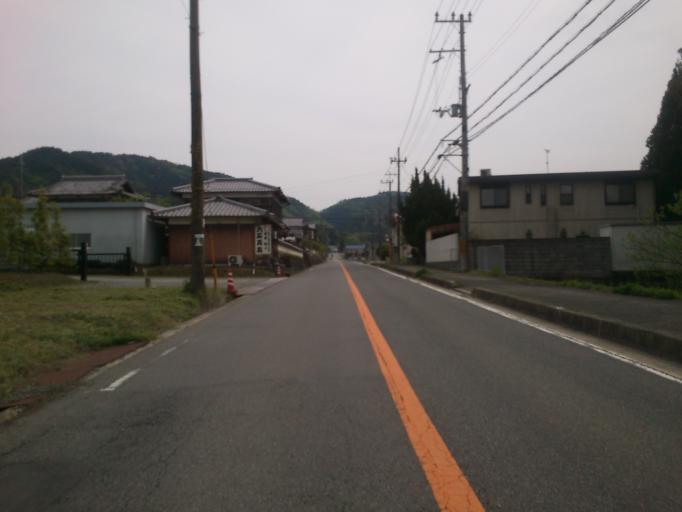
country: JP
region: Kyoto
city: Kameoka
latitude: 34.9886
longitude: 135.5466
